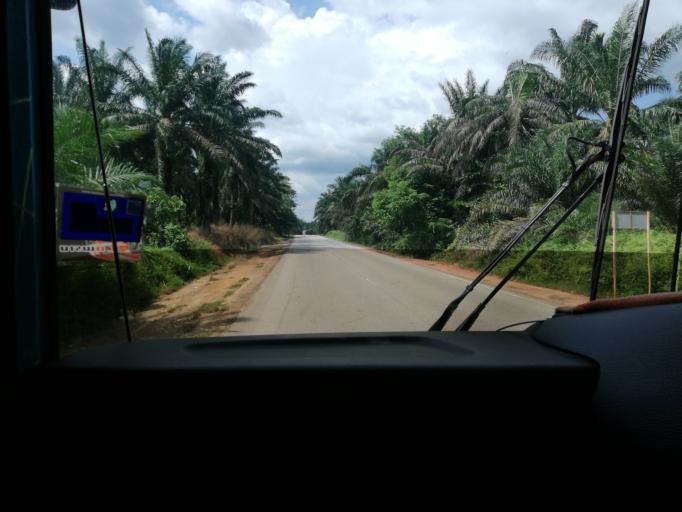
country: MY
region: Perak
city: Parit Buntar
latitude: 5.1504
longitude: 100.5920
